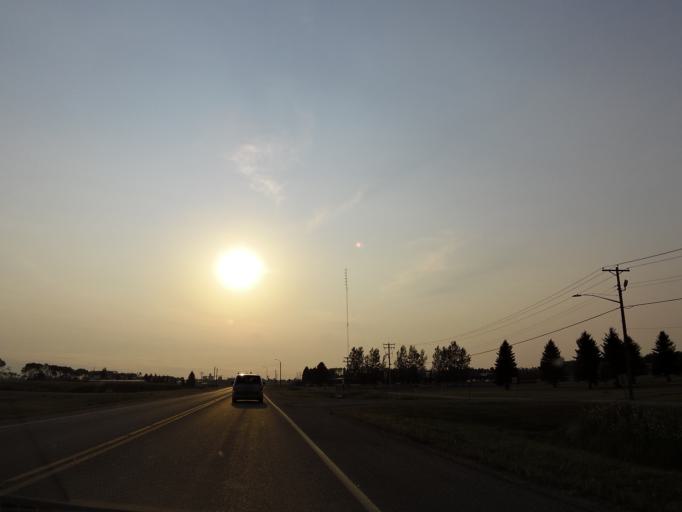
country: US
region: North Dakota
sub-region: Traill County
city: Mayville
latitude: 47.4985
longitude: -97.3452
